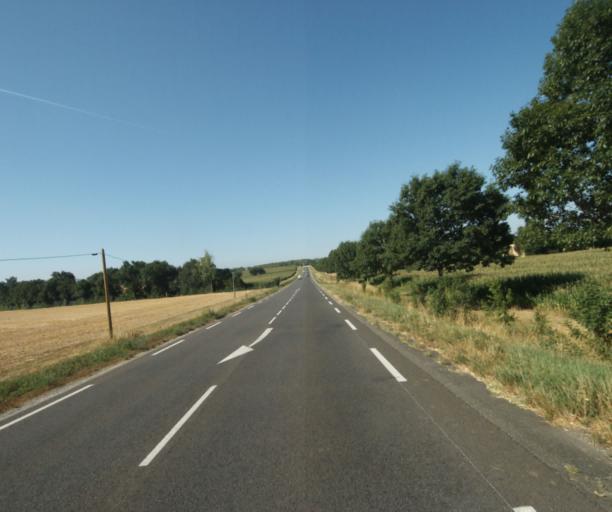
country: FR
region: Midi-Pyrenees
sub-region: Departement du Tarn
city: Soreze
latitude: 43.4948
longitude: 2.0425
